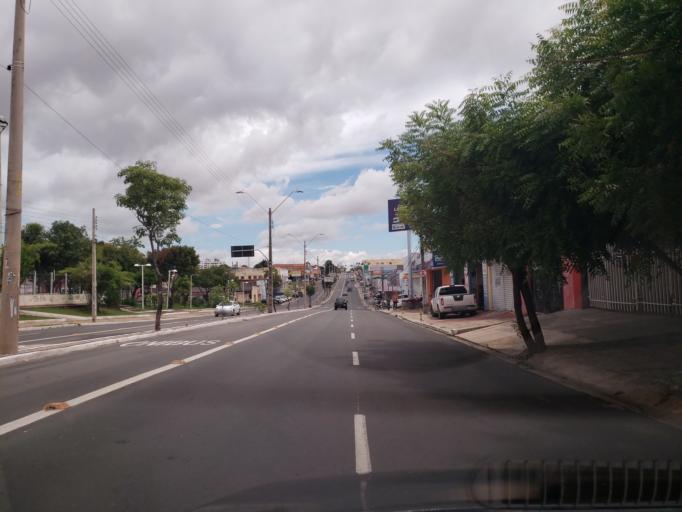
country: BR
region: Piaui
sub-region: Teresina
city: Teresina
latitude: -5.1100
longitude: -42.8074
